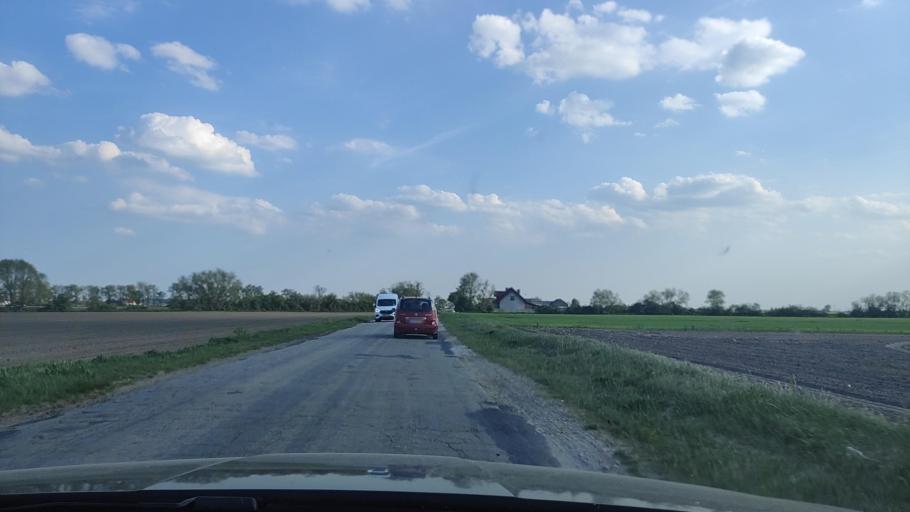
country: PL
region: Greater Poland Voivodeship
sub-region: Powiat poznanski
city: Kleszczewo
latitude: 52.3732
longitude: 17.1671
